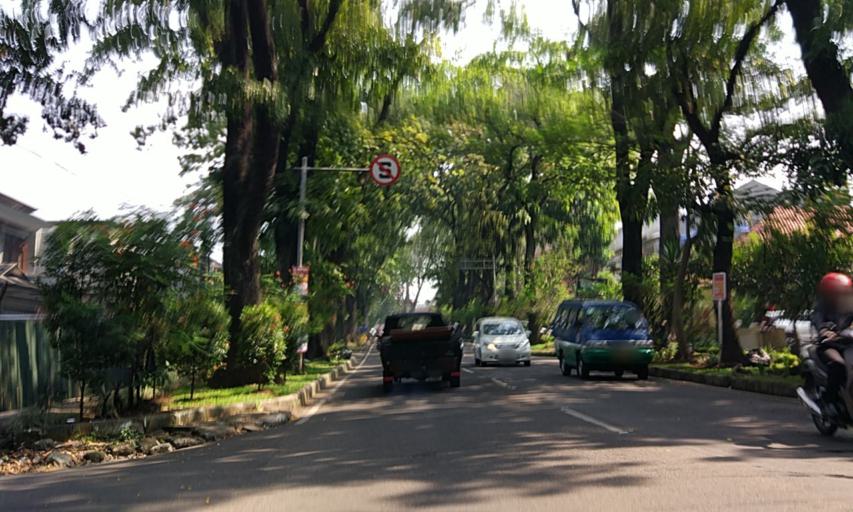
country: ID
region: West Java
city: Bandung
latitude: -6.9022
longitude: 107.5997
